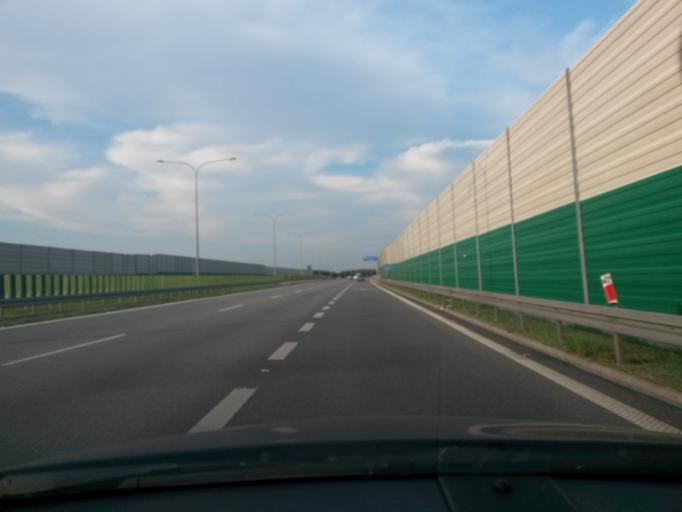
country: PL
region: Lodz Voivodeship
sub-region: powiat Lowicki
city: Bobrowniki
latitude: 52.0300
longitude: 20.0074
